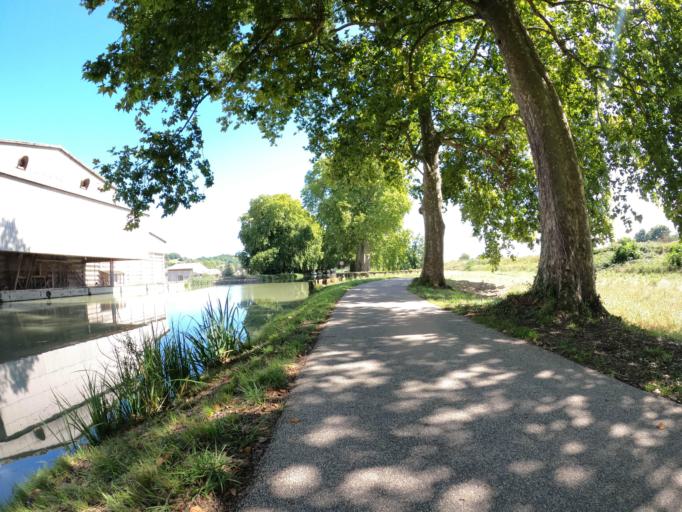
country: FR
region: Midi-Pyrenees
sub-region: Departement du Tarn-et-Garonne
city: Saint-Nicolas-de-la-Grave
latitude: 44.0898
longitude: 0.9636
